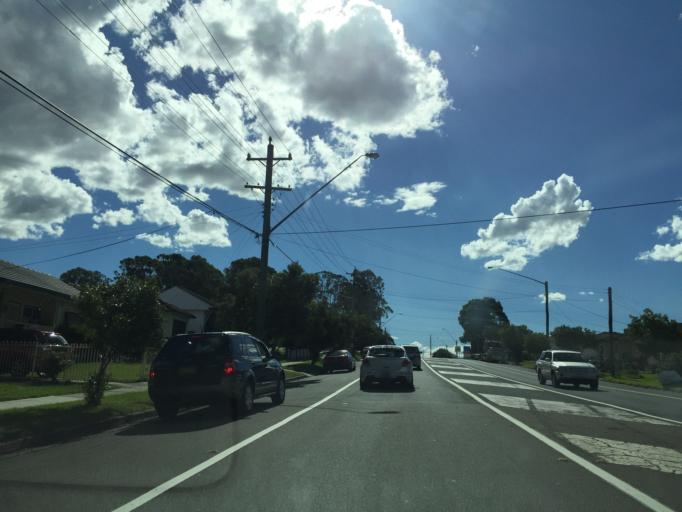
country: AU
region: New South Wales
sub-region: Parramatta
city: Constitution Hill
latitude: -33.7869
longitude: 150.9694
